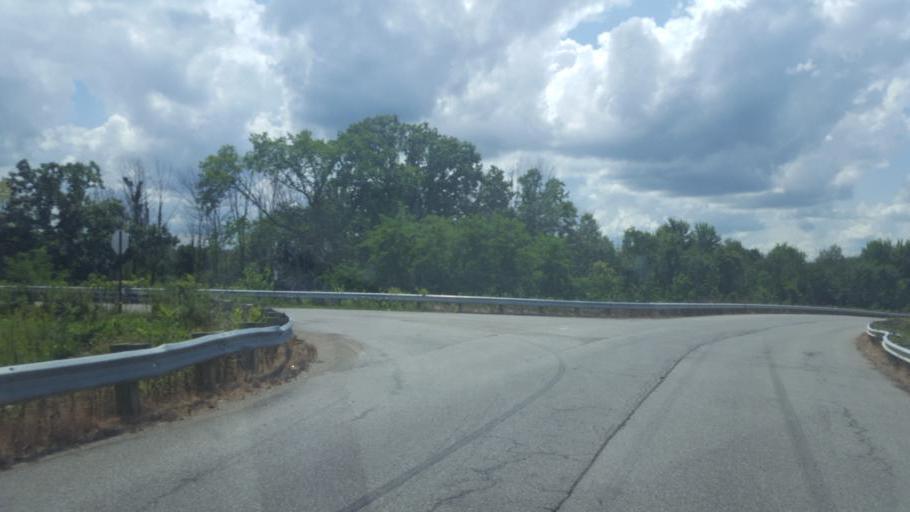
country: US
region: Ohio
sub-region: Morrow County
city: Mount Gilead
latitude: 40.4678
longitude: -82.7597
